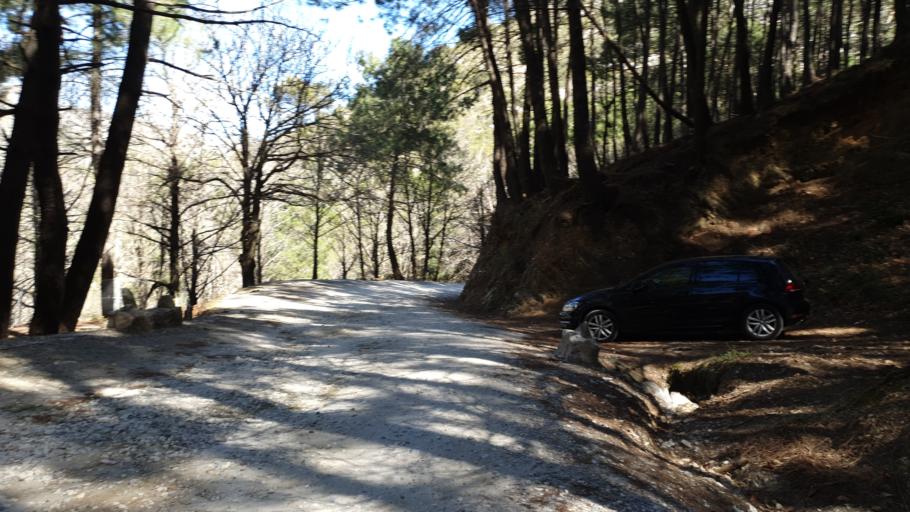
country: ES
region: Andalusia
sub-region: Provincia de Malaga
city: Ojen
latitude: 36.5771
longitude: -4.8841
